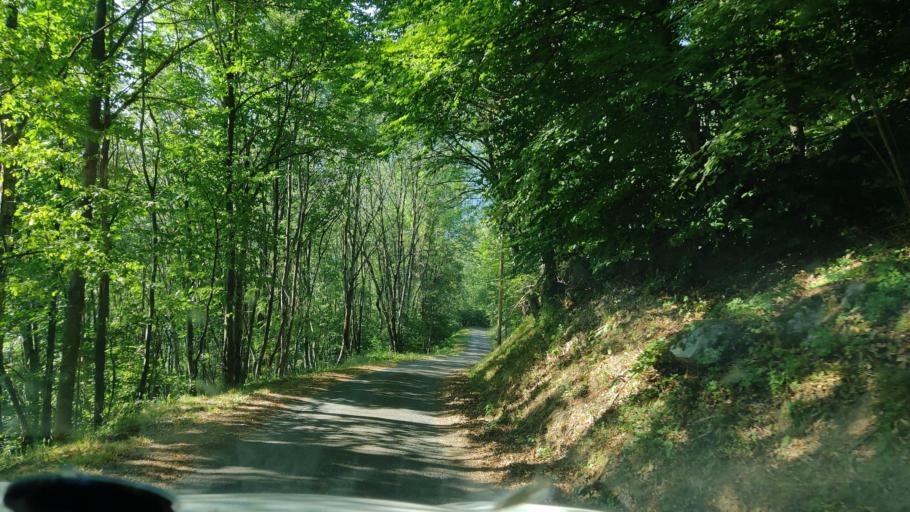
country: FR
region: Rhone-Alpes
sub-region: Departement de la Savoie
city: Saint-Etienne-de-Cuines
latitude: 45.3427
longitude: 6.2752
